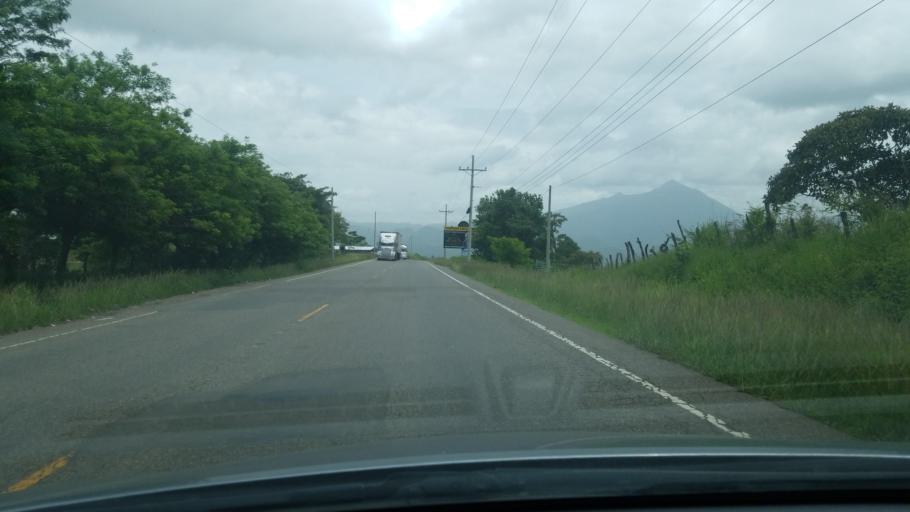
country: HN
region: Copan
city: Cucuyagua
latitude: 14.6701
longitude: -88.8477
